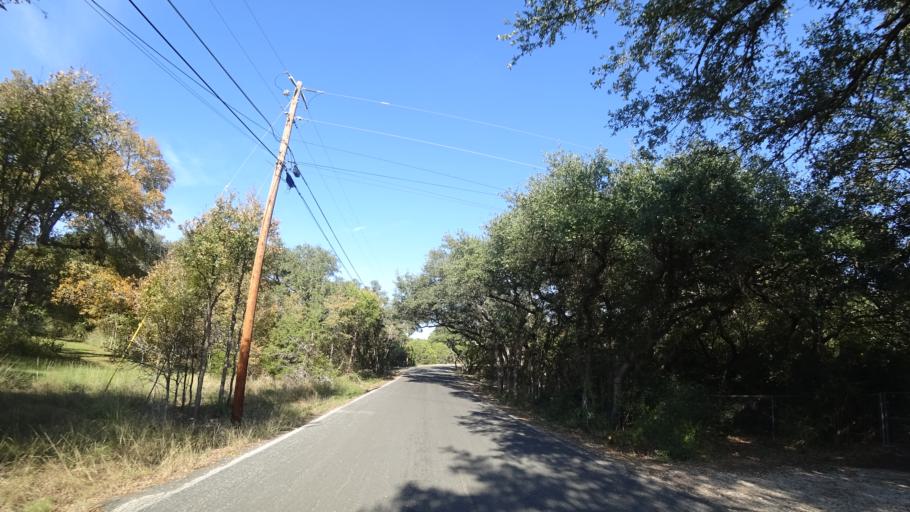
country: US
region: Texas
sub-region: Travis County
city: Barton Creek
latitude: 30.2362
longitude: -97.9247
